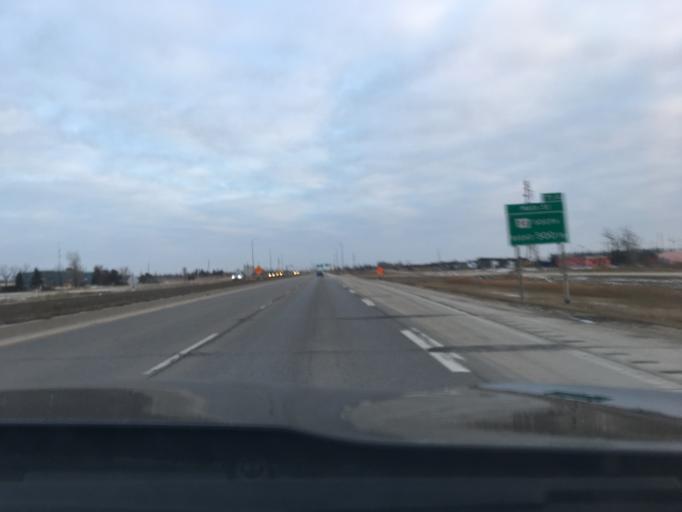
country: CA
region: Manitoba
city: Winnipeg
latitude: 49.9775
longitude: -97.0862
